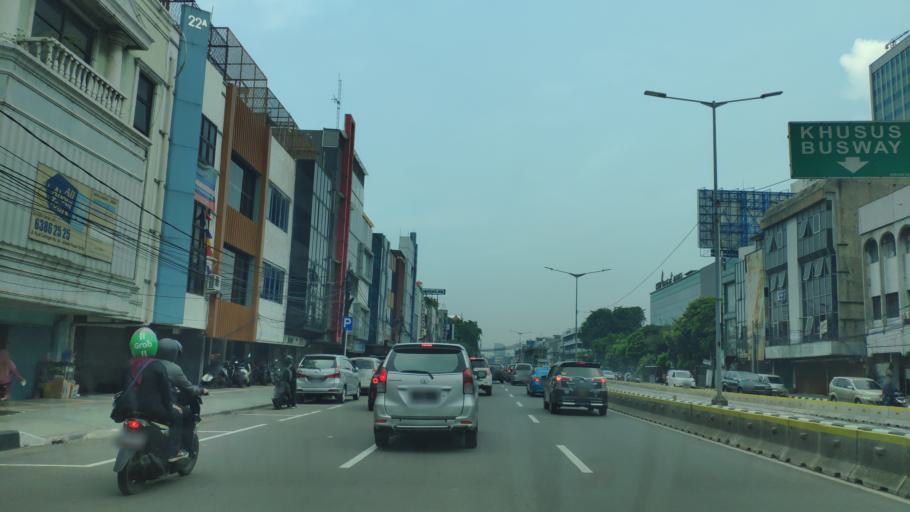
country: ID
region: Jakarta Raya
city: Jakarta
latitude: -6.1713
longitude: 106.8090
